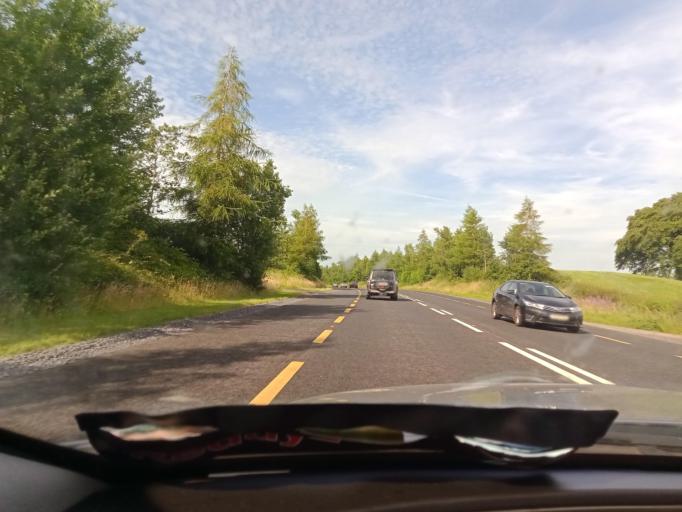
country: IE
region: Leinster
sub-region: An Iarmhi
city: An Muileann gCearr
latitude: 53.4897
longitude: -7.3371
